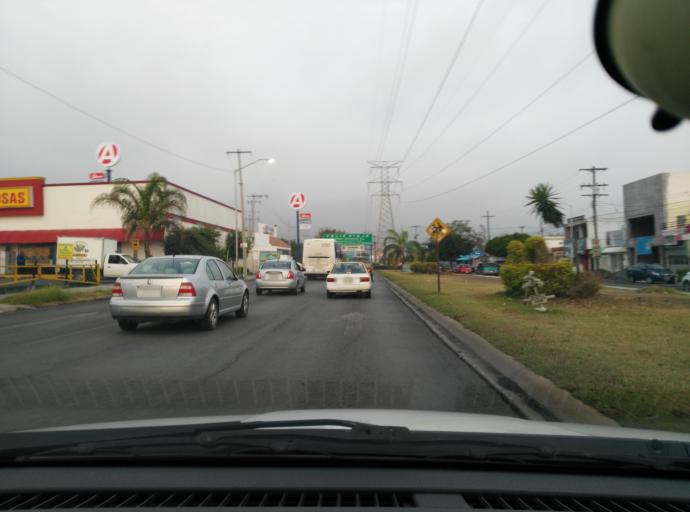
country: MX
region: Nuevo Leon
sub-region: San Nicolas de los Garza
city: San Nicolas de los Garza
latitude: 25.7710
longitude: -100.2654
